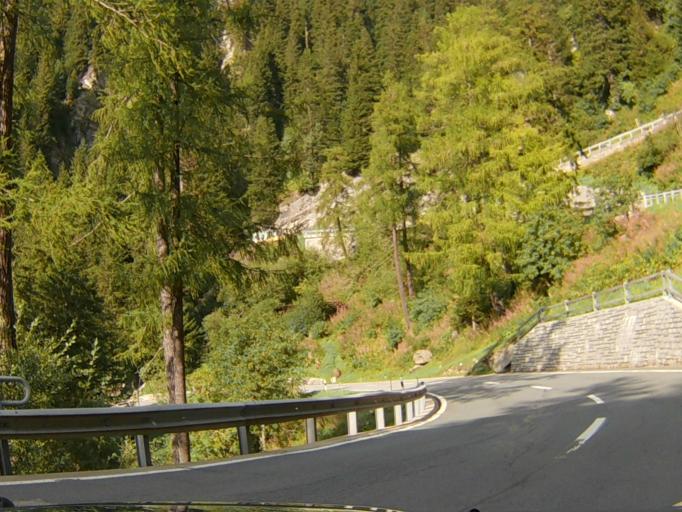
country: CH
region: Grisons
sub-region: Maloja District
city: Silvaplana
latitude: 46.3959
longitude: 9.6902
